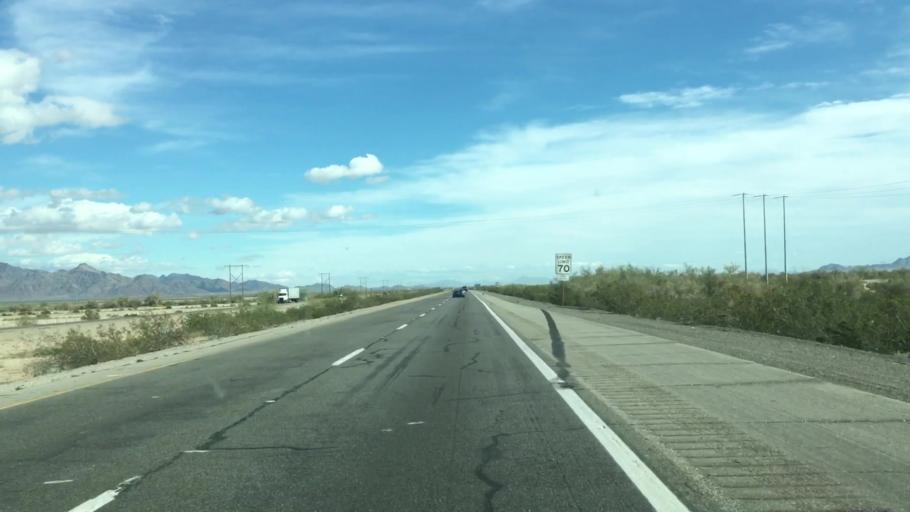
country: US
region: California
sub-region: Riverside County
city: Mesa Verde
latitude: 33.6059
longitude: -114.9800
